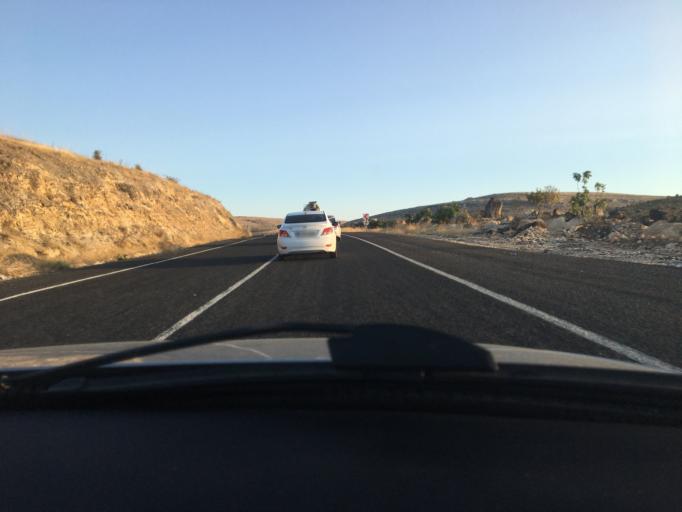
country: TR
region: Sanliurfa
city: Halfeti
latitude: 37.1929
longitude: 37.9673
